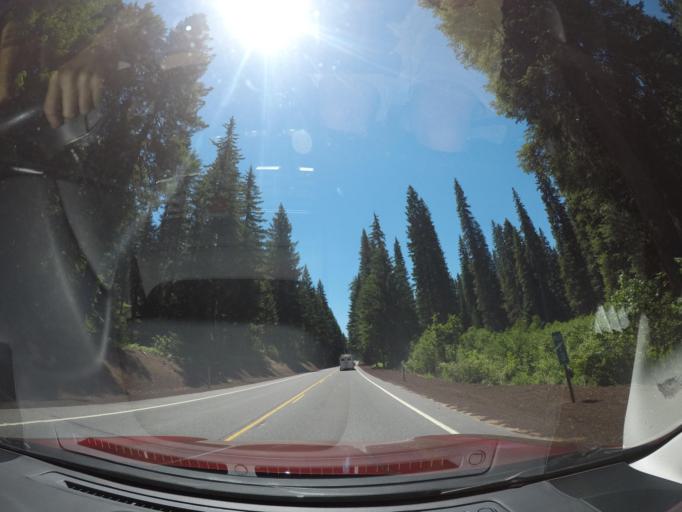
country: US
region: Oregon
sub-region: Deschutes County
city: Sisters
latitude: 44.5385
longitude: -121.9951
